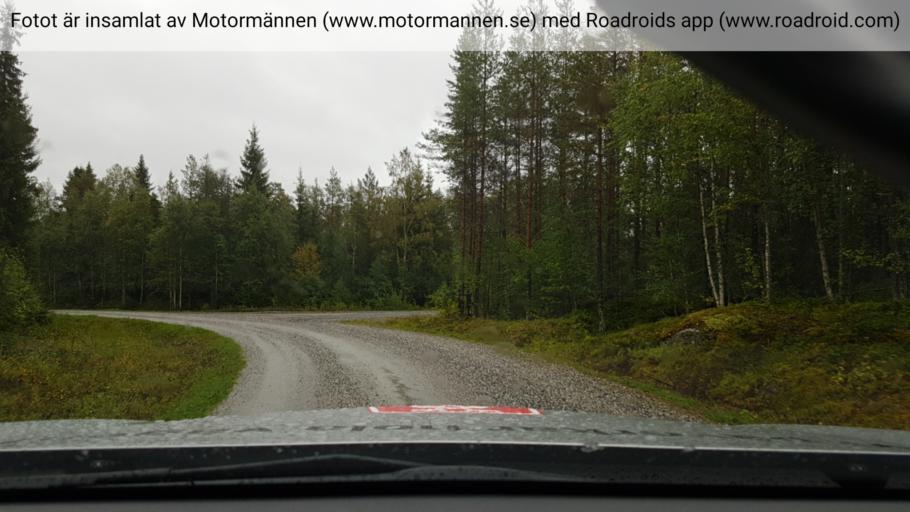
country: SE
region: Vaesterbotten
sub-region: Asele Kommun
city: Asele
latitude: 63.9793
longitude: 17.5809
